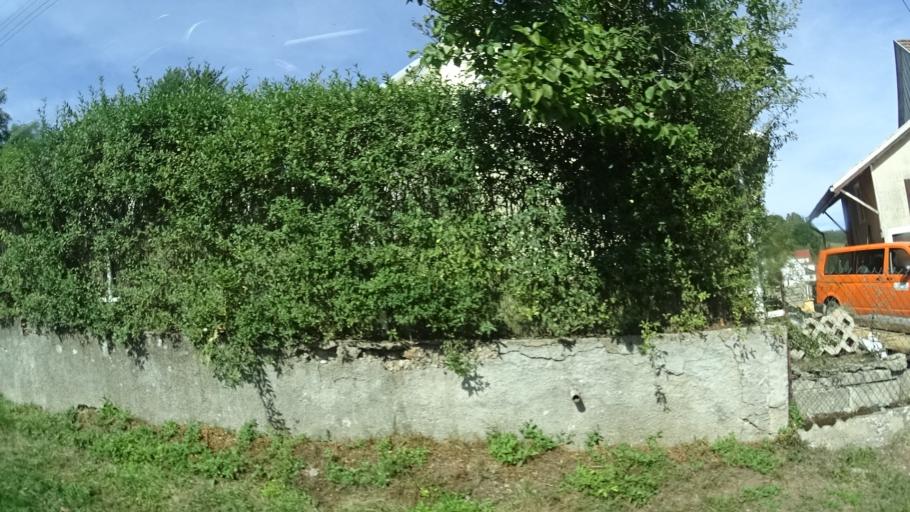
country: DE
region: Thuringia
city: Christes
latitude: 50.6611
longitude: 10.4769
